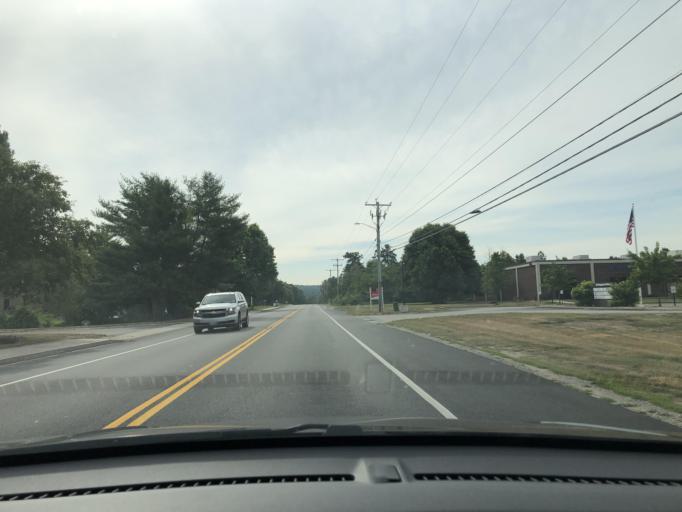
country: US
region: New Hampshire
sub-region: Merrimack County
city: Concord
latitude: 43.2117
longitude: -71.4952
